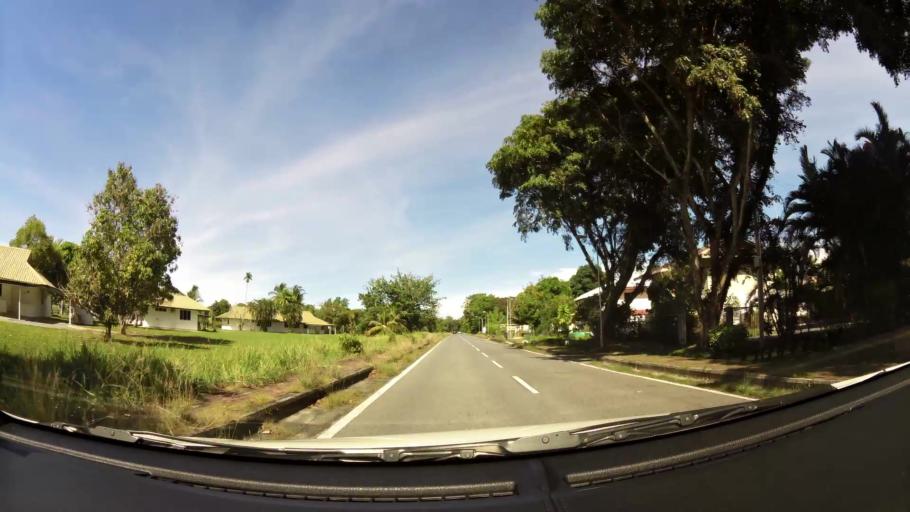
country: BN
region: Belait
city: Kuala Belait
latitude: 4.5865
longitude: 114.1973
